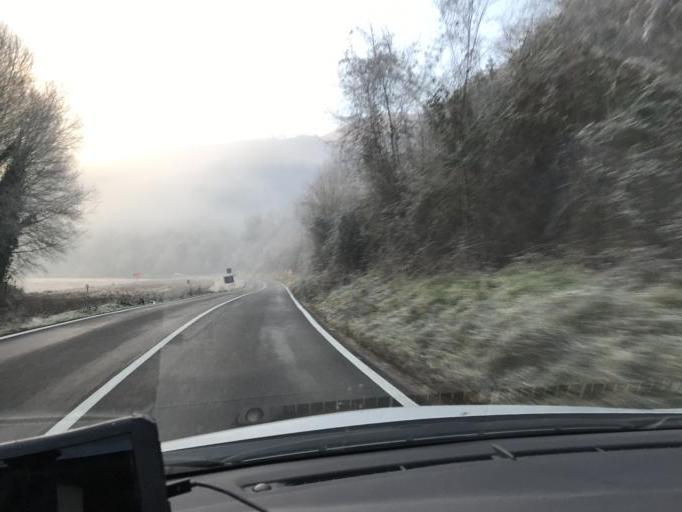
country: IT
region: Latium
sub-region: Provincia di Rieti
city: Colli sul Velino
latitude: 42.5222
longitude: 12.7344
